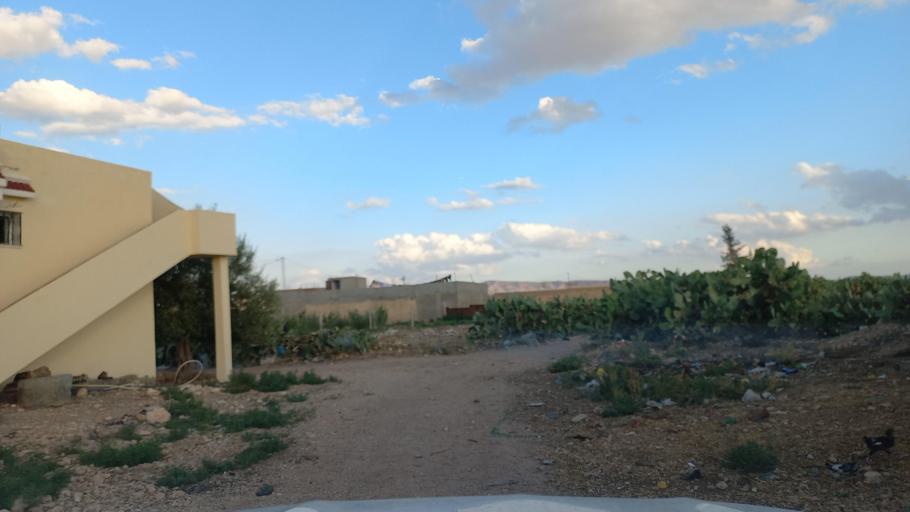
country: TN
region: Al Qasrayn
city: Sbiba
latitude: 35.3759
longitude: 9.0545
